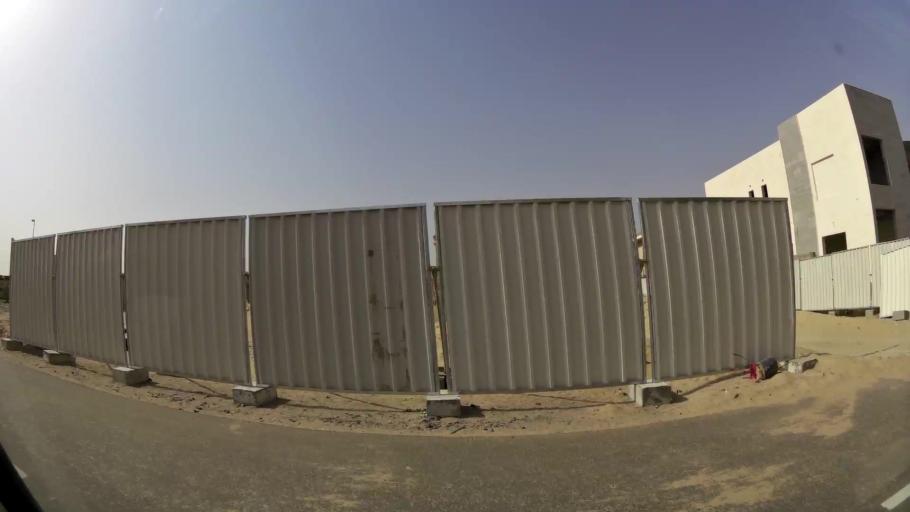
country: AE
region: Ash Shariqah
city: Sharjah
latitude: 25.2624
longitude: 55.4601
